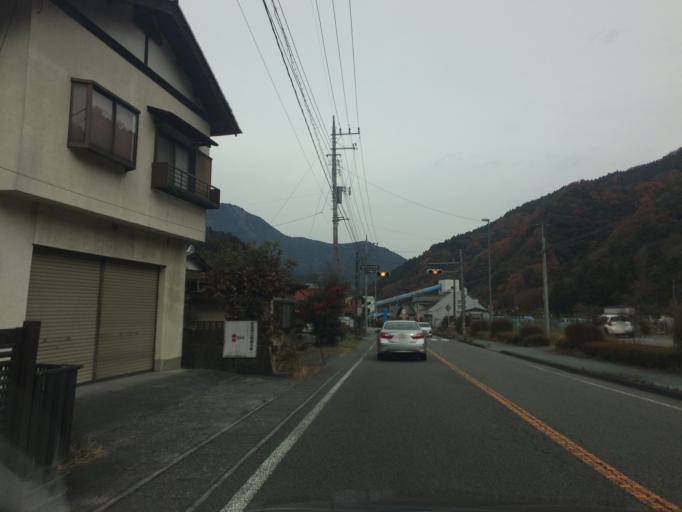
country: JP
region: Shizuoka
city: Fujinomiya
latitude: 35.3503
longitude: 138.4215
